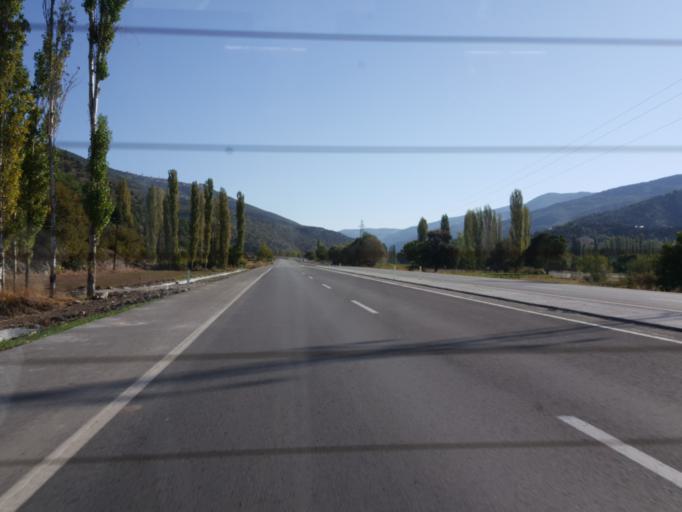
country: TR
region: Tokat
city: Turhal
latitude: 40.4759
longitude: 36.1476
